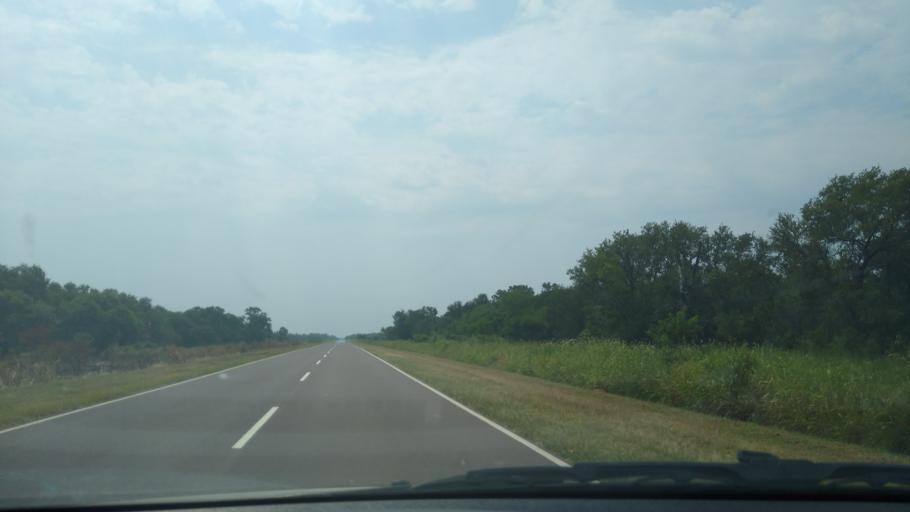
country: AR
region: Chaco
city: La Eduvigis
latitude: -27.0408
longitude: -58.9637
